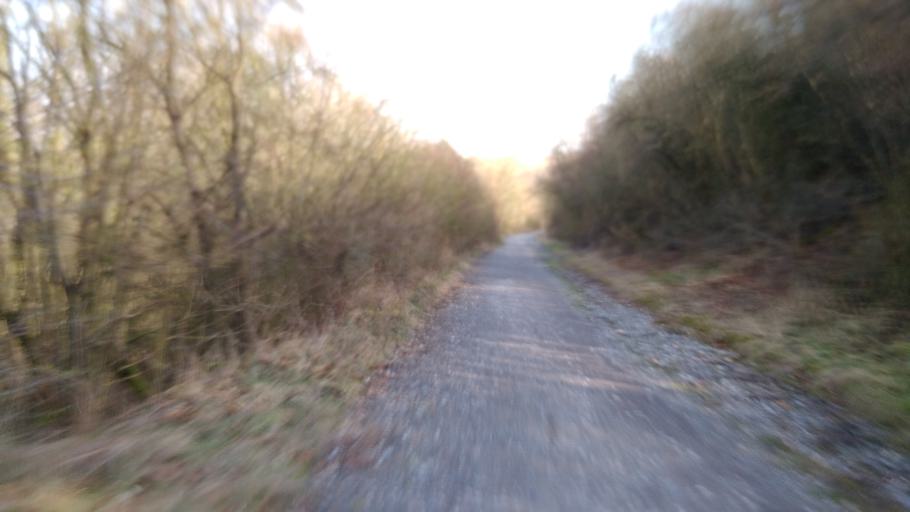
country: DE
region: North Rhine-Westphalia
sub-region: Regierungsbezirk Munster
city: Bottrop
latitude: 51.5566
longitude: 6.8797
